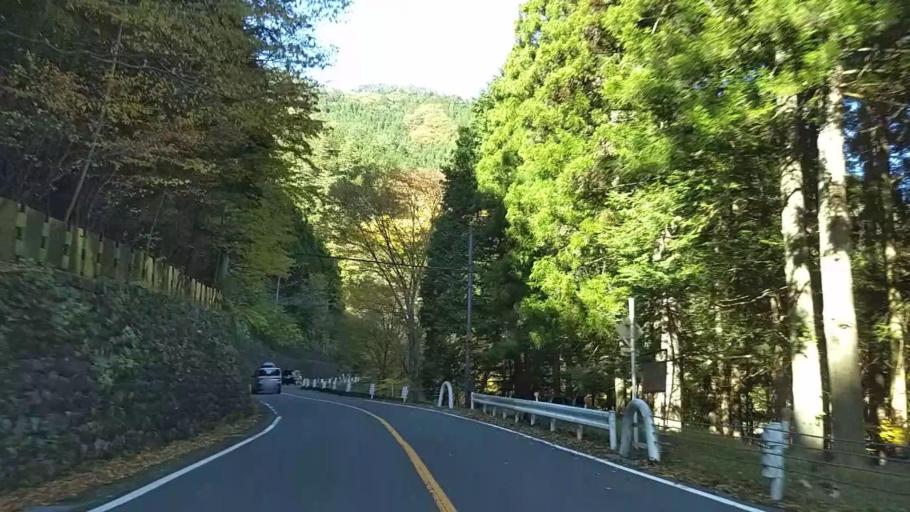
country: JP
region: Yamanashi
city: Otsuki
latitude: 35.7634
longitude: 138.9930
